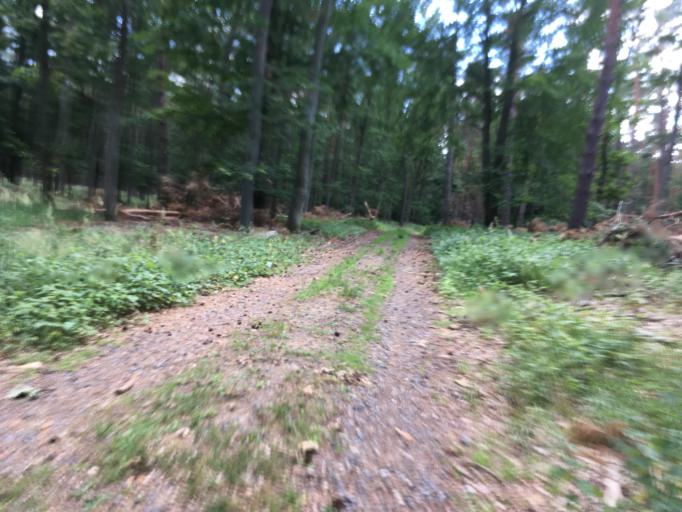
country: DE
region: Brandenburg
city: Joachimsthal
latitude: 52.9123
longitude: 13.7428
